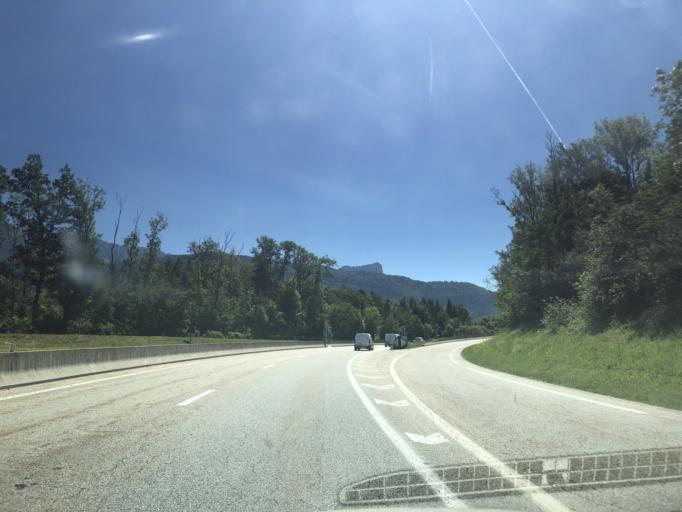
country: FR
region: Rhone-Alpes
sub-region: Departement de la Haute-Savoie
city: Villaz
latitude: 45.9356
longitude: 6.1689
